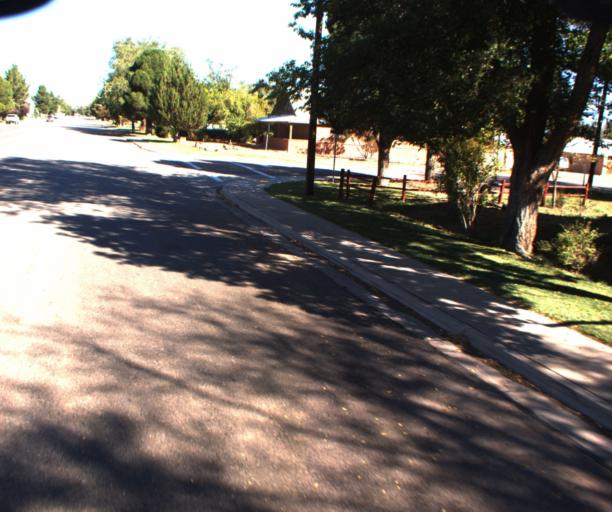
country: US
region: Arizona
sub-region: Coconino County
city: Fredonia
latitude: 36.9470
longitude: -112.5263
